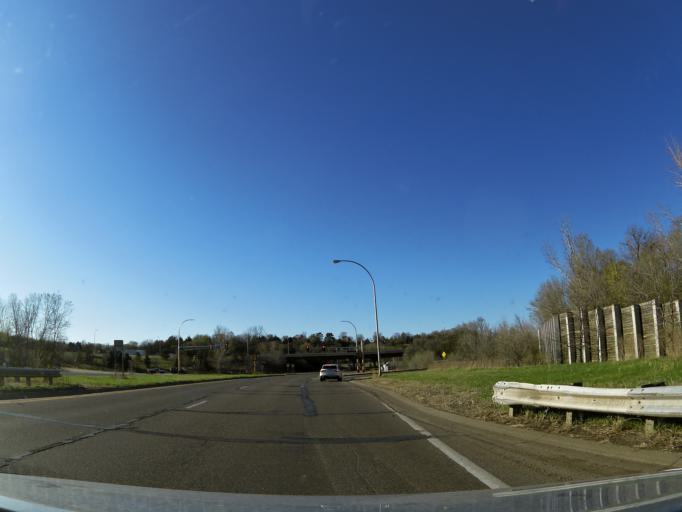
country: US
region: Minnesota
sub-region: Washington County
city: Lakeland
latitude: 44.9597
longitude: -92.7725
